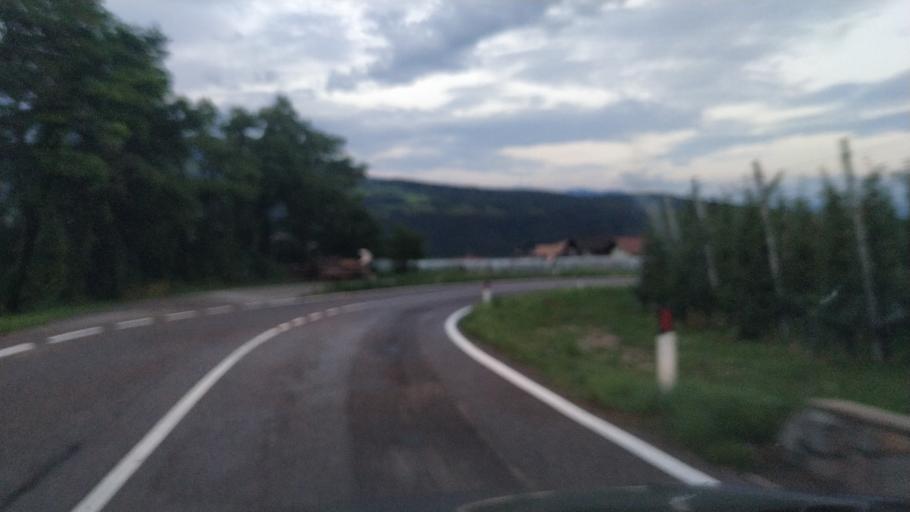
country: IT
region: Trentino-Alto Adige
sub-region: Provincia di Trento
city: Brez
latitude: 46.4350
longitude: 11.1090
